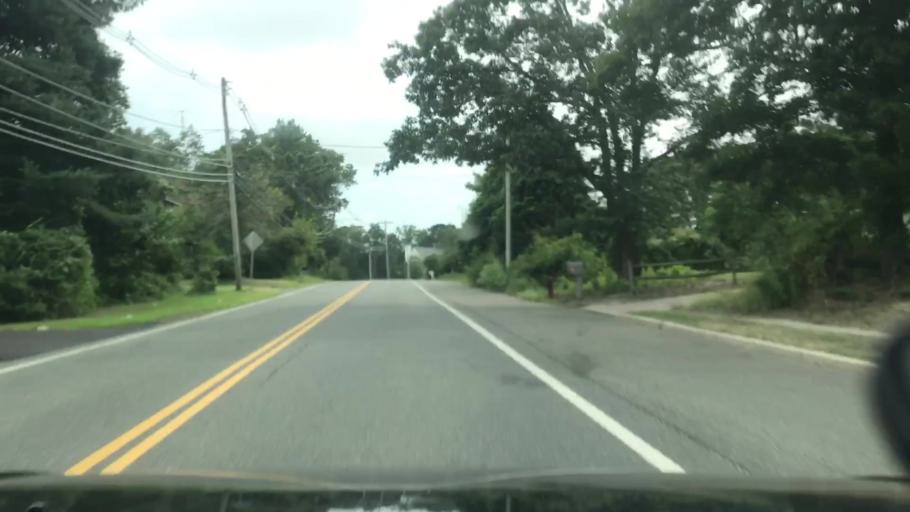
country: US
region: New Jersey
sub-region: Ocean County
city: Barnegat
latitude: 39.7532
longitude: -74.2393
